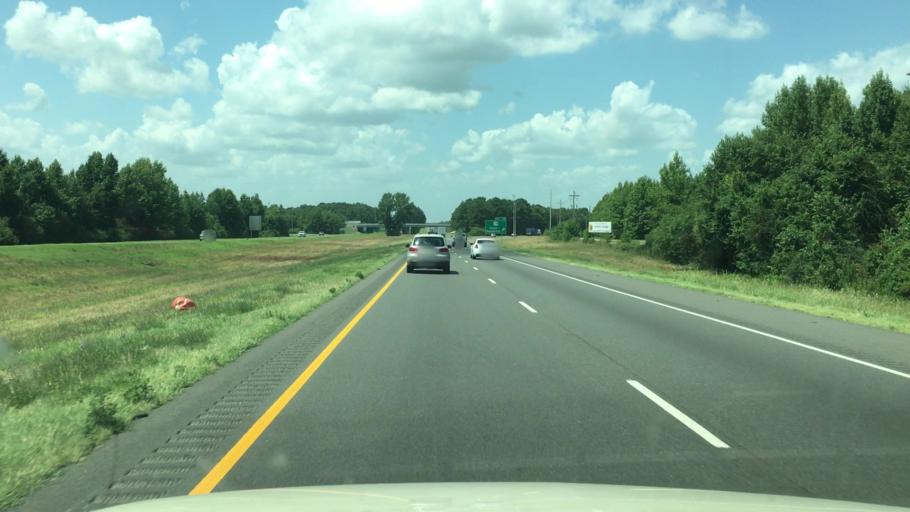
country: US
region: Arkansas
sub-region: Hempstead County
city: Hope
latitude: 33.6867
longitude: -93.6044
